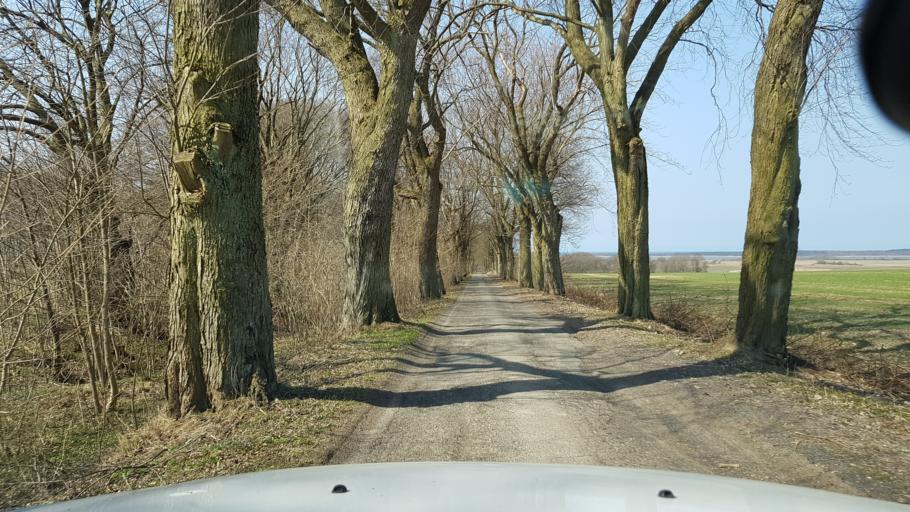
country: PL
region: West Pomeranian Voivodeship
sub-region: Powiat slawienski
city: Darlowo
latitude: 54.4661
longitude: 16.4977
